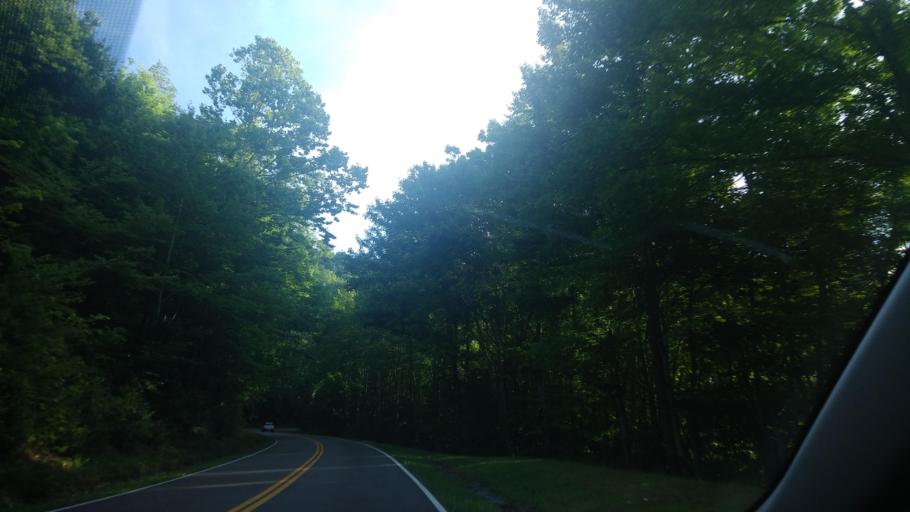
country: US
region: Tennessee
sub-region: Cocke County
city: Newport
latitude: 35.8059
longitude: -83.2382
